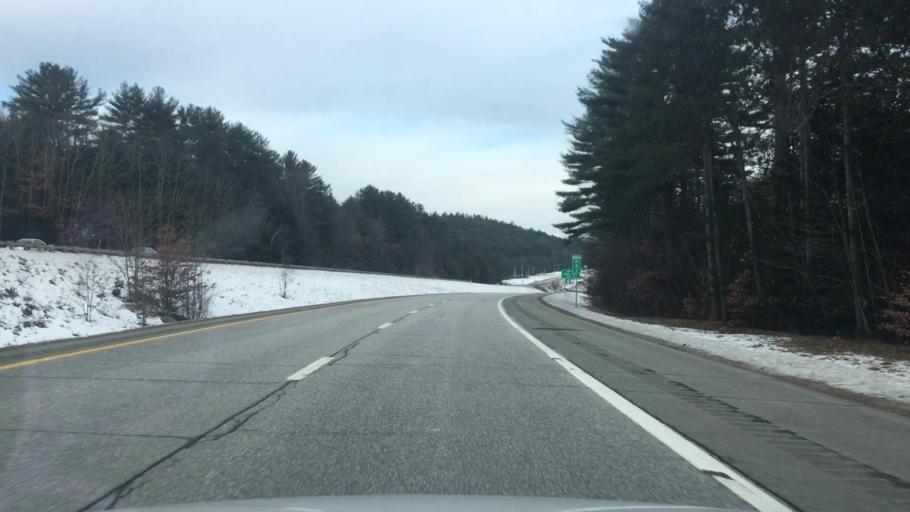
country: US
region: New Hampshire
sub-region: Merrimack County
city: Henniker
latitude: 43.2836
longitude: -71.8330
